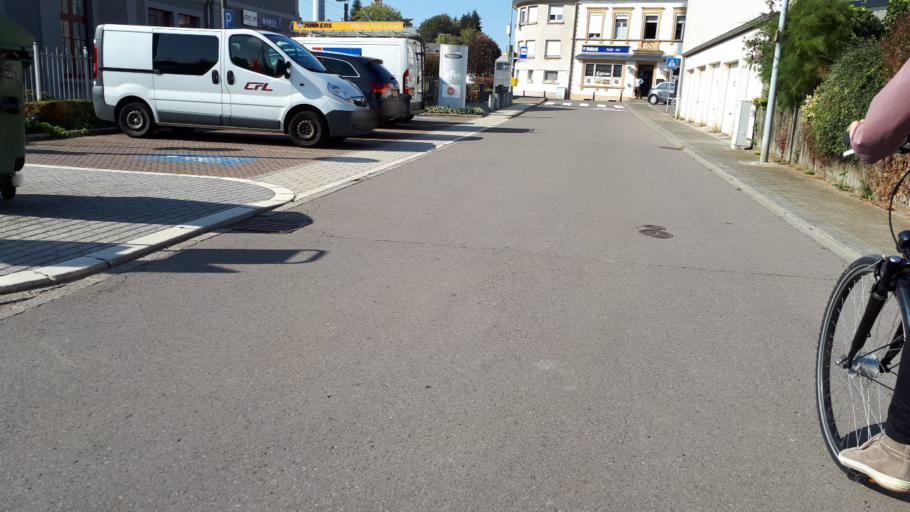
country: LU
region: Luxembourg
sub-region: Canton de Capellen
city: Mamer
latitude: 49.6257
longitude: 6.0207
